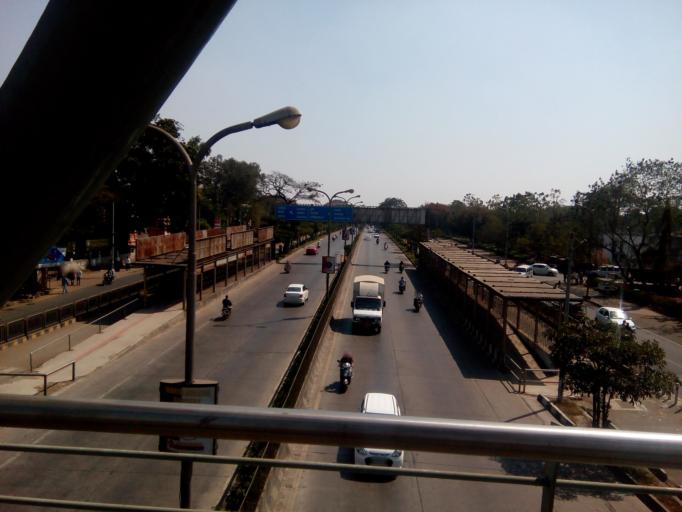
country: IN
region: Maharashtra
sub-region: Pune Division
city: Pimpri
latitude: 18.6237
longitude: 73.8079
